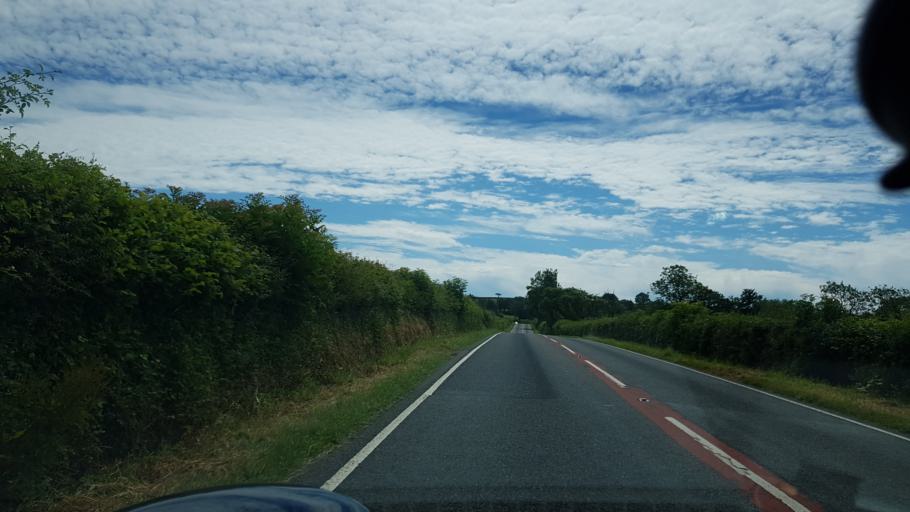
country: GB
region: Wales
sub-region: Carmarthenshire
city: Saint Clears
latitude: 51.7933
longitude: -4.4849
